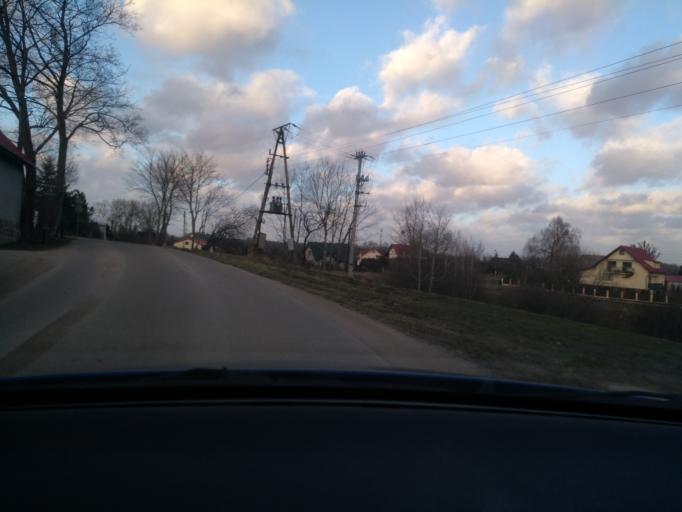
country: PL
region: Pomeranian Voivodeship
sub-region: Powiat kartuski
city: Przodkowo
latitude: 54.4166
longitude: 18.2800
